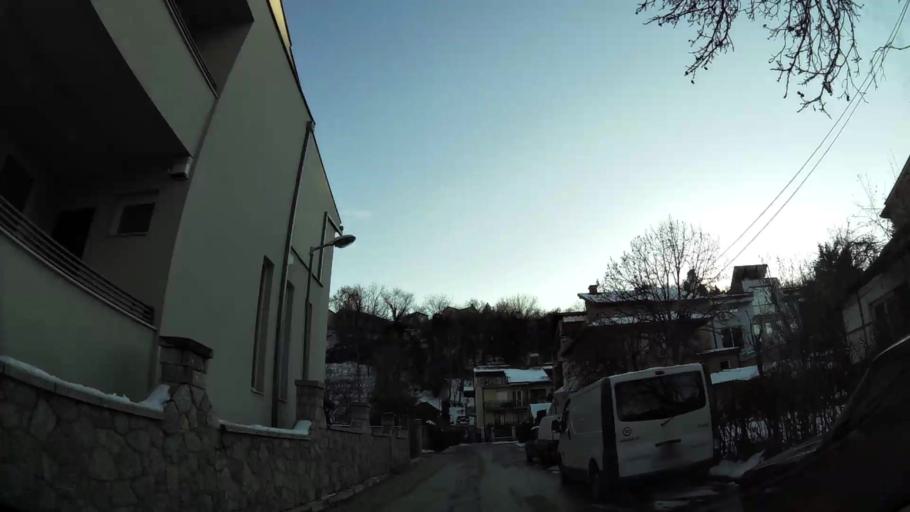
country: MK
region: Karpos
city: Skopje
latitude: 41.9920
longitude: 21.4026
